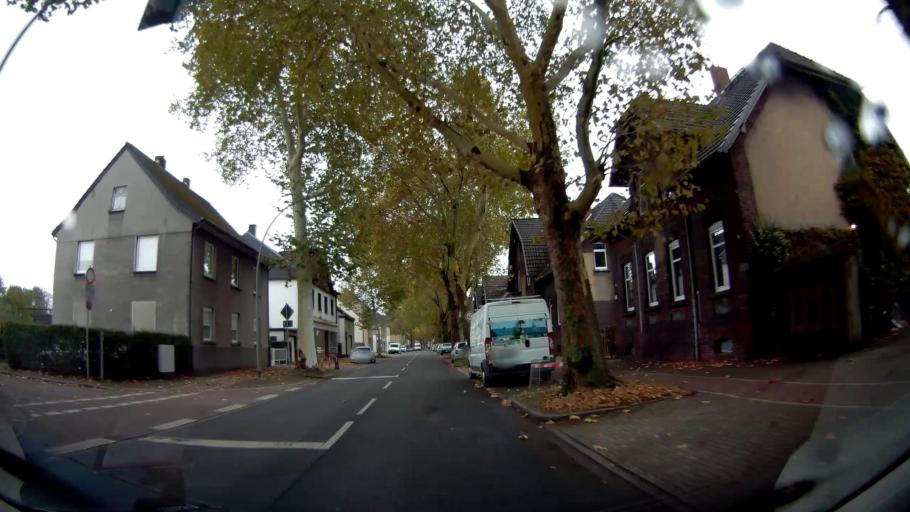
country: DE
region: North Rhine-Westphalia
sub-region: Regierungsbezirk Munster
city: Bottrop
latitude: 51.5367
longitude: 6.9528
